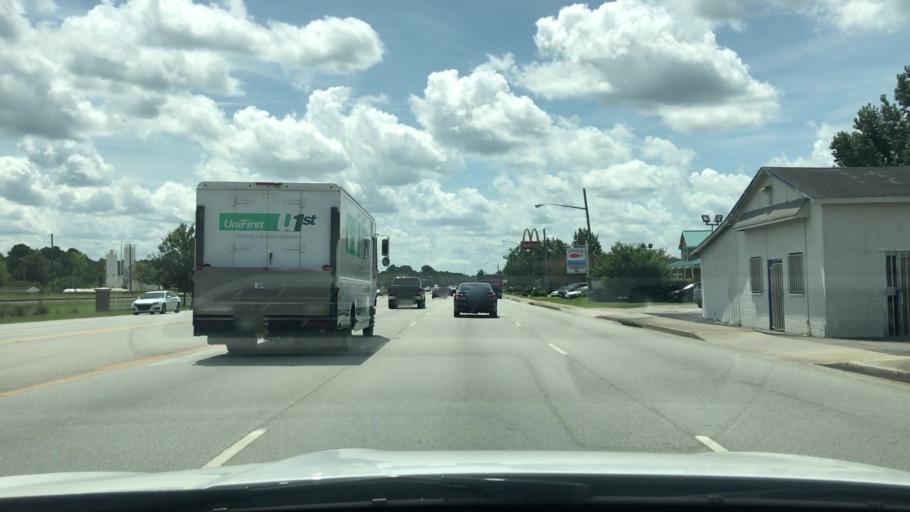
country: US
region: South Carolina
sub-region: Berkeley County
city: Goose Creek
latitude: 33.0002
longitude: -80.0383
